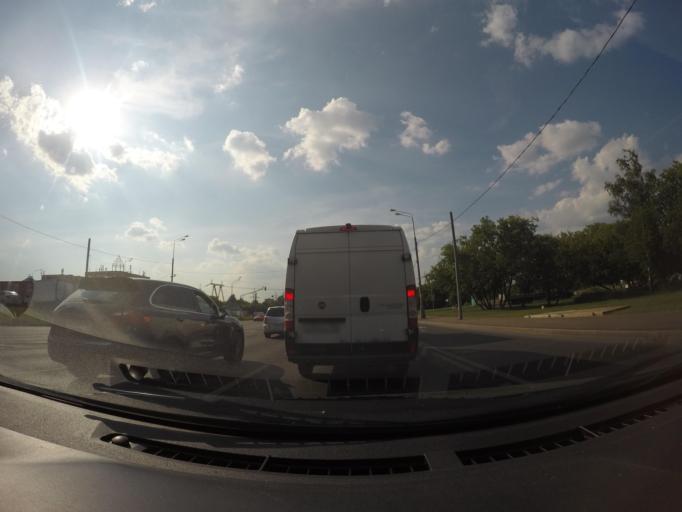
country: RU
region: Moscow
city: Zhulebino
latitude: 55.7048
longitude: 37.8446
